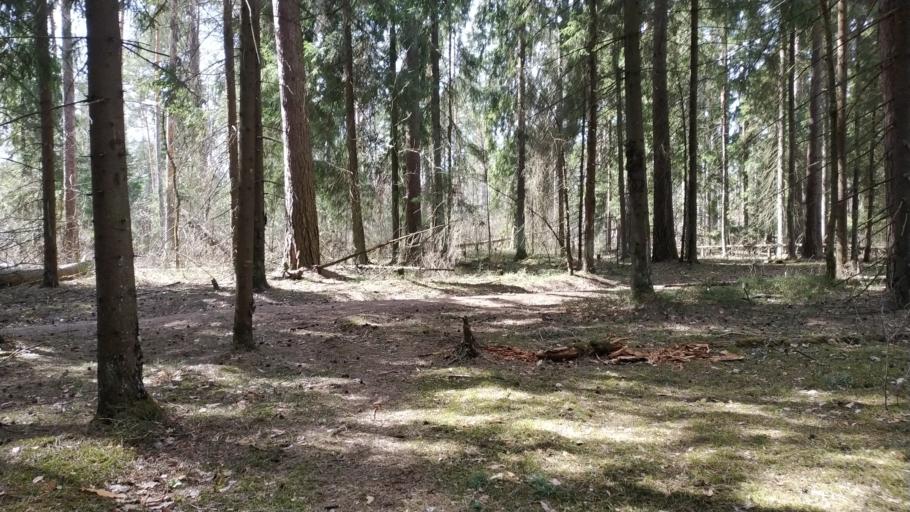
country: RU
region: Moskovskaya
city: Malyshevo
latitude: 55.5457
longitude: 38.3355
